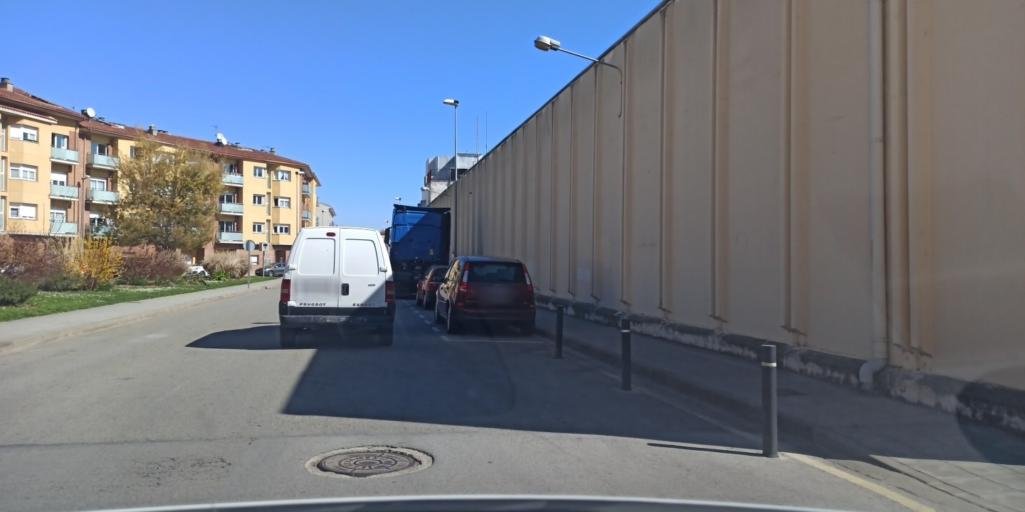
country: ES
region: Catalonia
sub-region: Provincia de Girona
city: Olot
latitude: 42.1703
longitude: 2.4756
